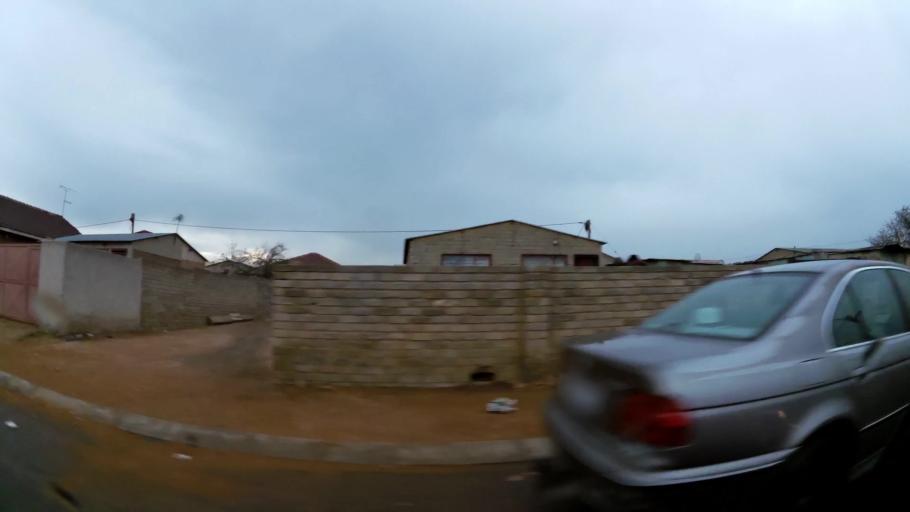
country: ZA
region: Gauteng
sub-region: City of Johannesburg Metropolitan Municipality
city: Roodepoort
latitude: -26.1780
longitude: 27.7886
